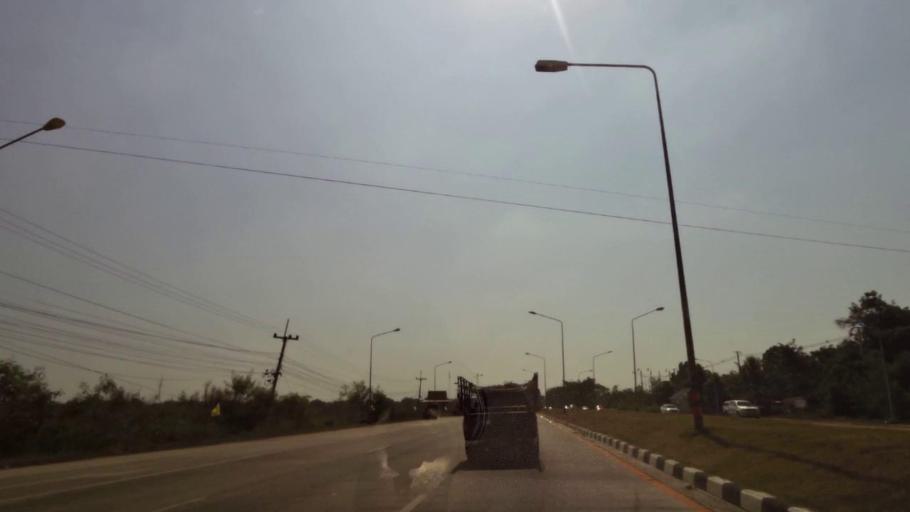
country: TH
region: Phichit
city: Wachira Barami
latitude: 16.3544
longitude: 100.1289
